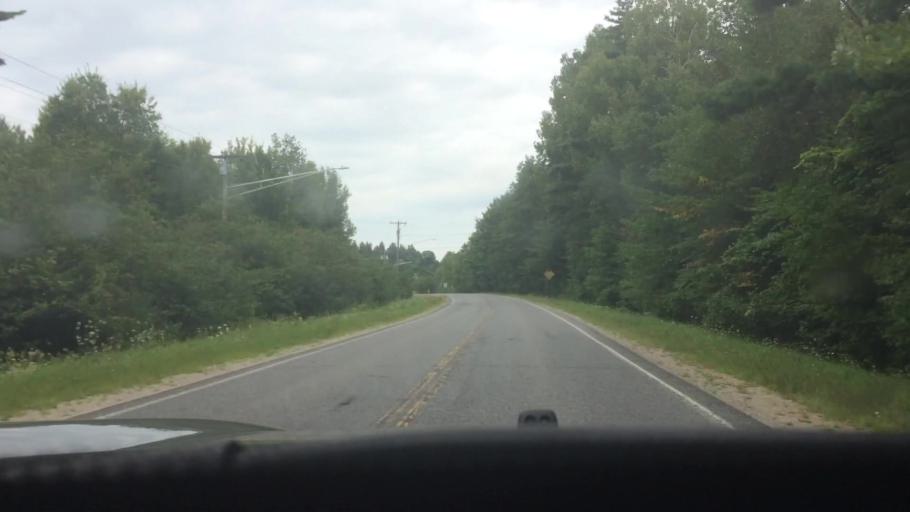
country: US
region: New York
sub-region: St. Lawrence County
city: Hannawa Falls
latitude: 44.5495
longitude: -74.9302
